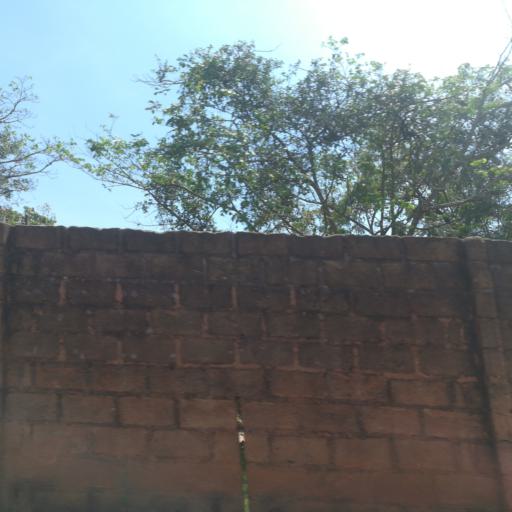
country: NG
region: Plateau
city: Bukuru
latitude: 9.8416
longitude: 8.9035
